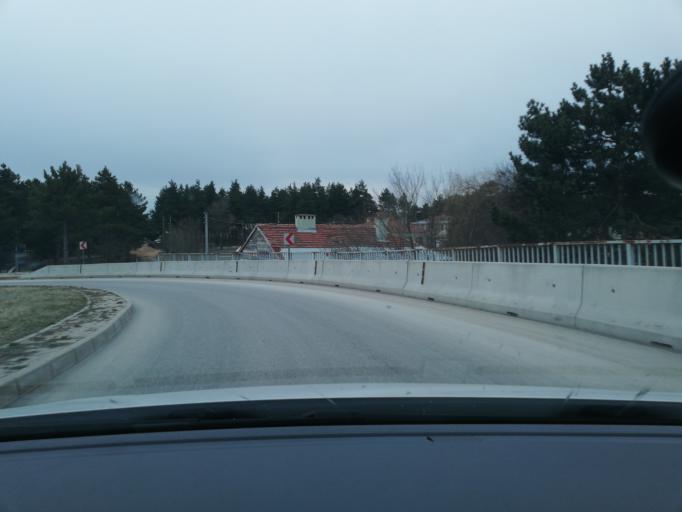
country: TR
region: Bolu
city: Gerede
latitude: 40.7942
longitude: 32.2049
